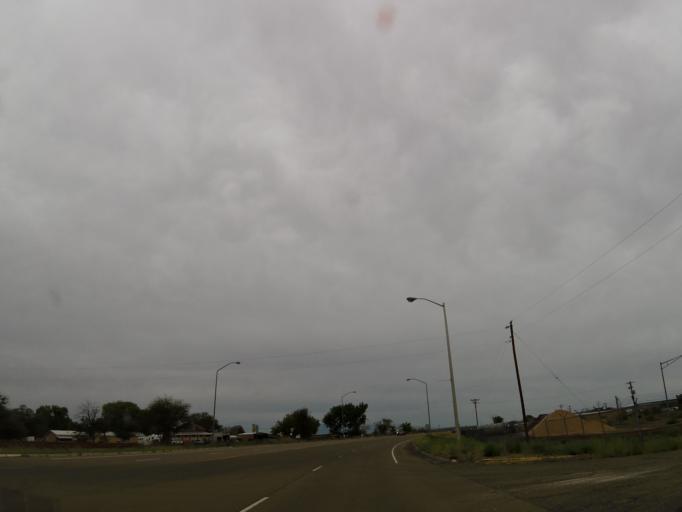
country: US
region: New Mexico
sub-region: Sandoval County
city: Jemez Pueblo
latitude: 35.5554
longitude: -106.7798
